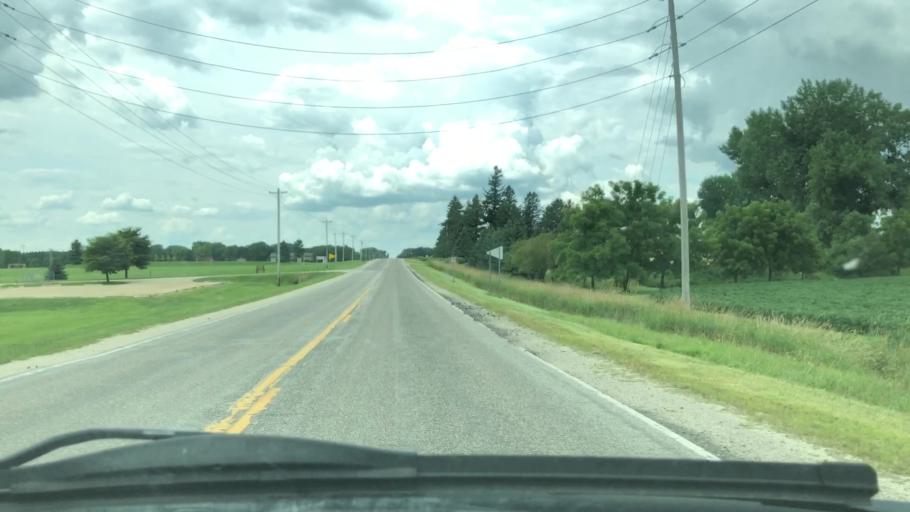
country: US
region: Minnesota
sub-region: Olmsted County
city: Stewartville
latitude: 43.8628
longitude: -92.4971
